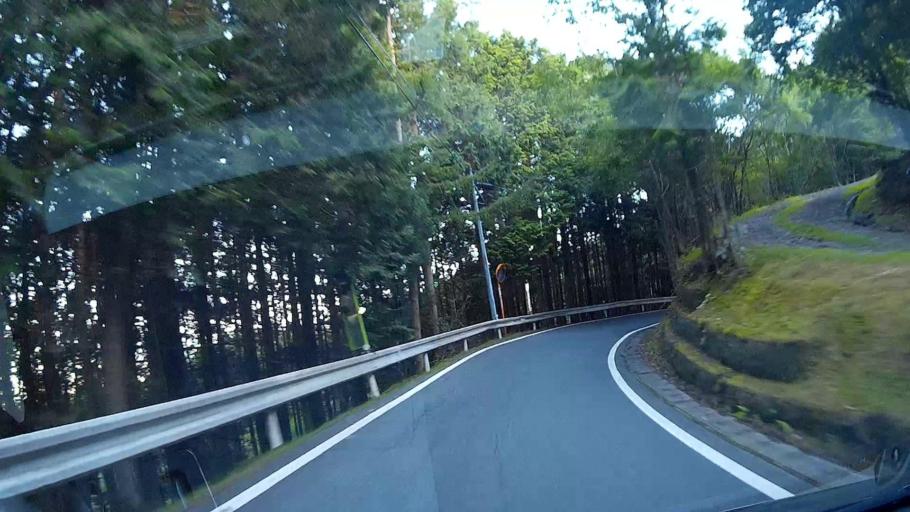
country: JP
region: Shizuoka
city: Shizuoka-shi
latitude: 35.1821
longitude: 138.2495
